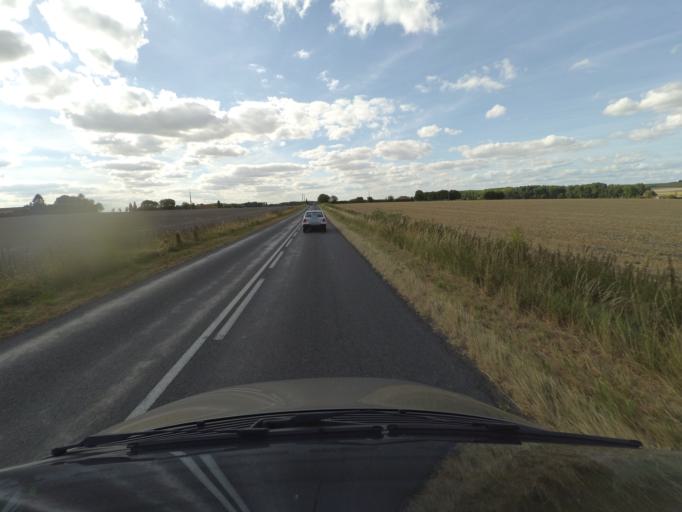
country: FR
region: Poitou-Charentes
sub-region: Departement de la Vienne
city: Saint-Gervais-les-Trois-Clochers
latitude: 46.9624
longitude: 0.3858
